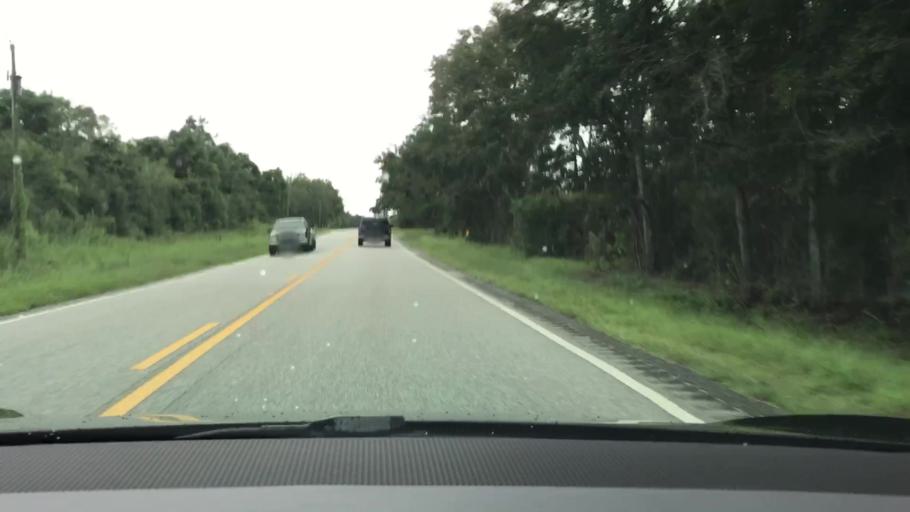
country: US
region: Alabama
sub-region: Geneva County
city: Samson
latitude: 31.0120
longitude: -86.1268
